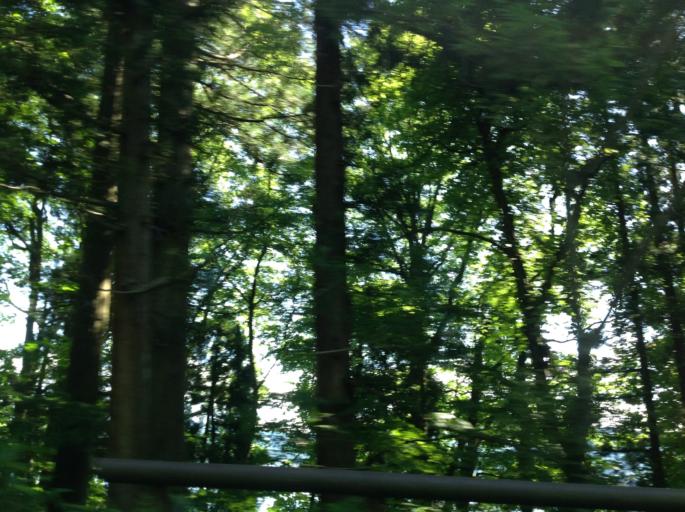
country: JP
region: Akita
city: Kakunodatemachi
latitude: 39.6985
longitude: 140.6484
